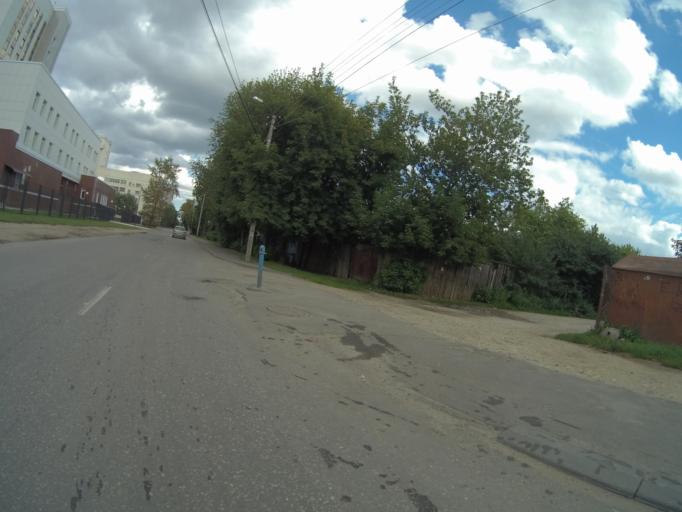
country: RU
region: Vladimir
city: Vladimir
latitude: 56.1178
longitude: 40.3639
